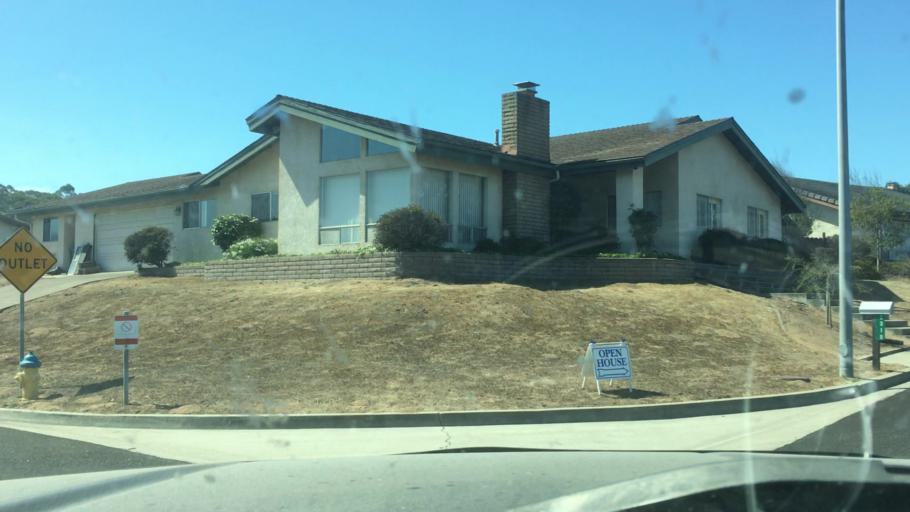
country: US
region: California
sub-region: San Luis Obispo County
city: Los Osos
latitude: 35.3079
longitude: -120.8251
